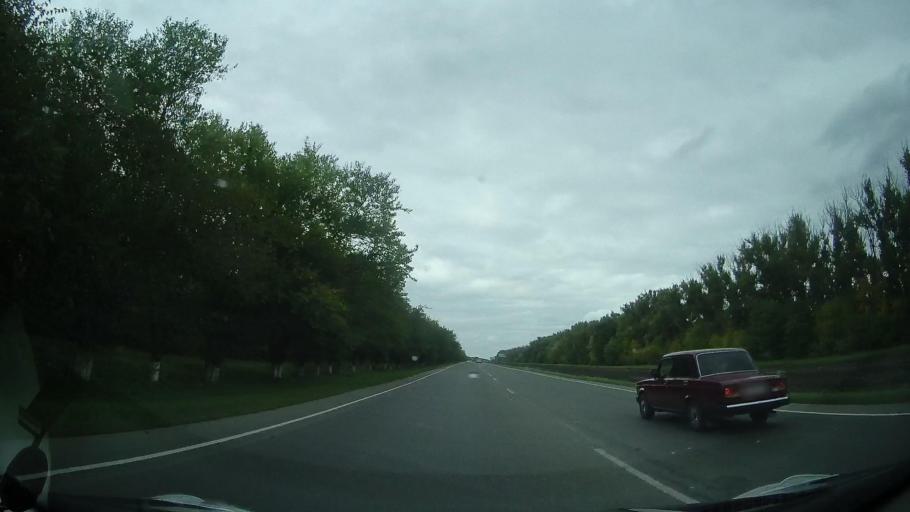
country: RU
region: Rostov
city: Yegorlykskaya
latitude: 46.6088
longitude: 40.6095
